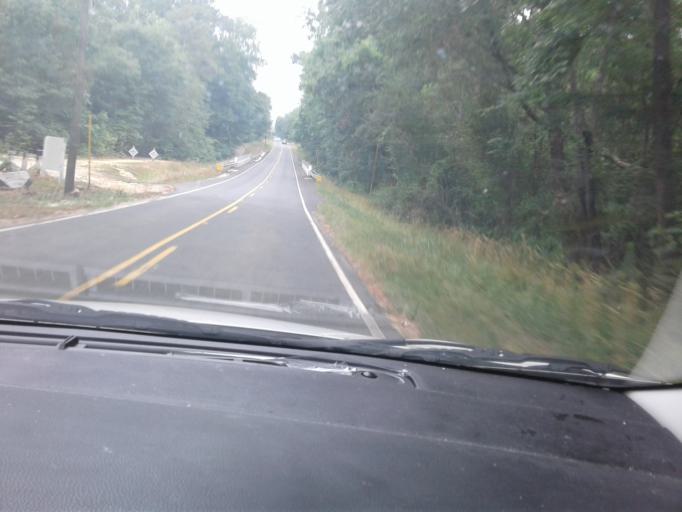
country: US
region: North Carolina
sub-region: Harnett County
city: Buies Creek
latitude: 35.4117
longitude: -78.7270
